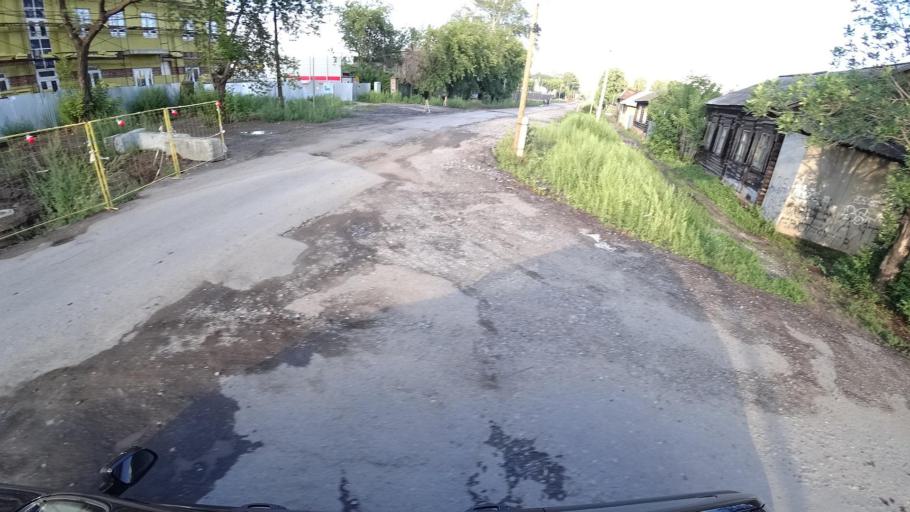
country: RU
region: Sverdlovsk
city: Kamyshlov
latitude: 56.8485
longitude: 62.7068
